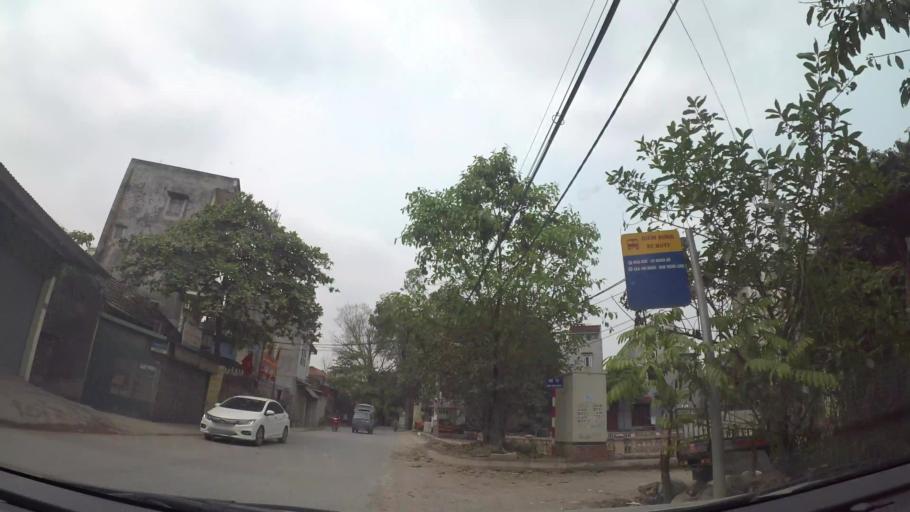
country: VN
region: Ha Noi
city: Cau Dien
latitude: 21.0382
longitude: 105.7380
